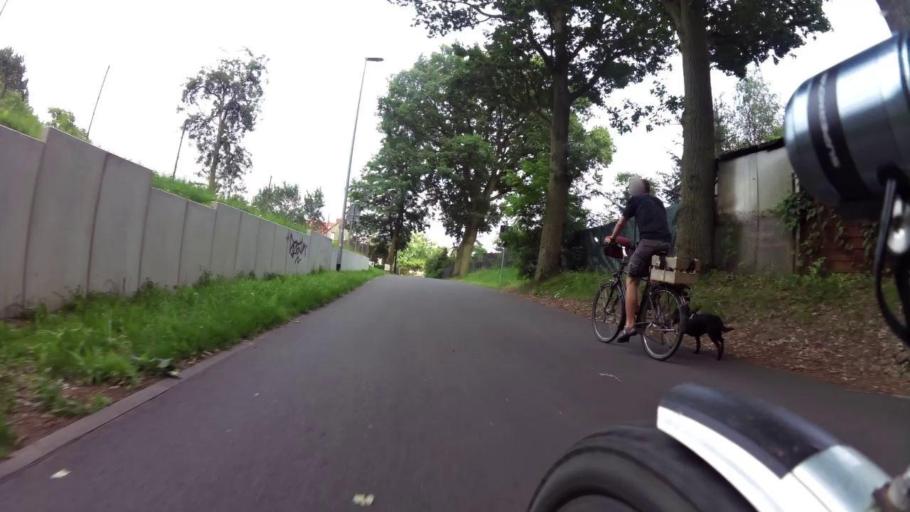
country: PL
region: West Pomeranian Voivodeship
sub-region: Powiat goleniowski
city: Stepnica
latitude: 53.6632
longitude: 14.4959
